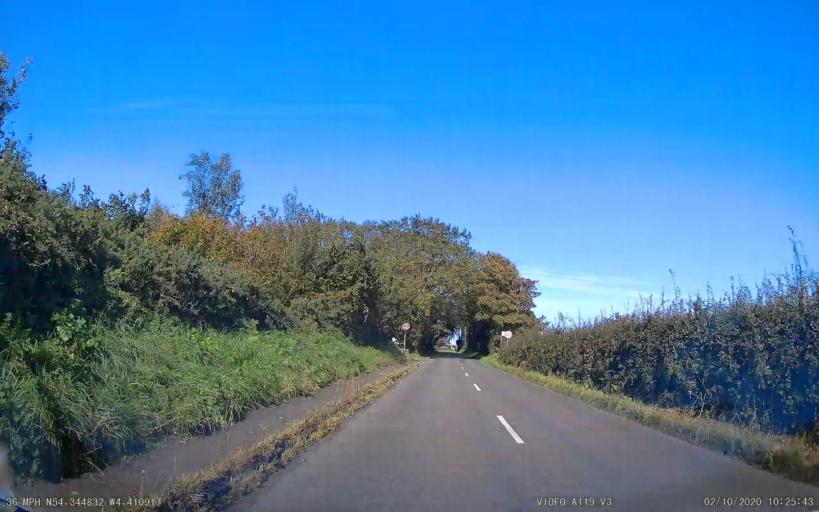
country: IM
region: Ramsey
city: Ramsey
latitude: 54.3448
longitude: -4.4109
